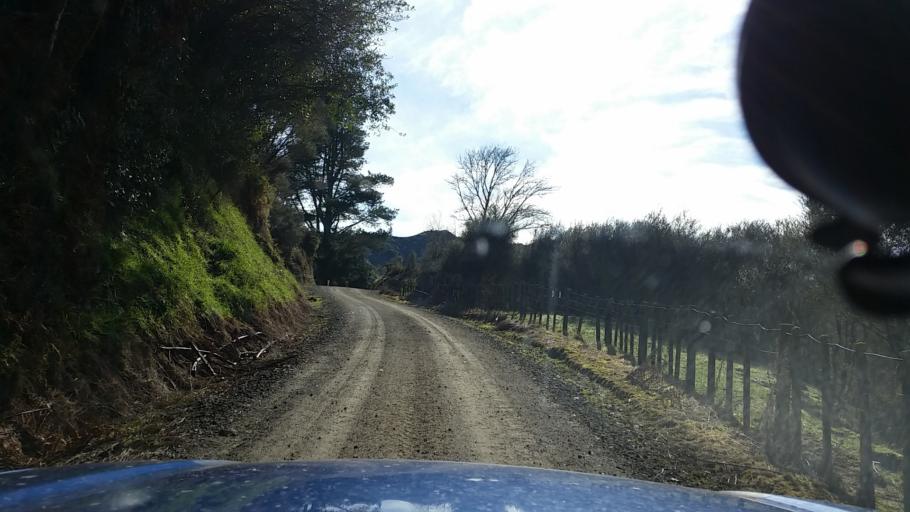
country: NZ
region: Taranaki
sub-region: New Plymouth District
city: Waitara
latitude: -39.0560
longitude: 174.7731
